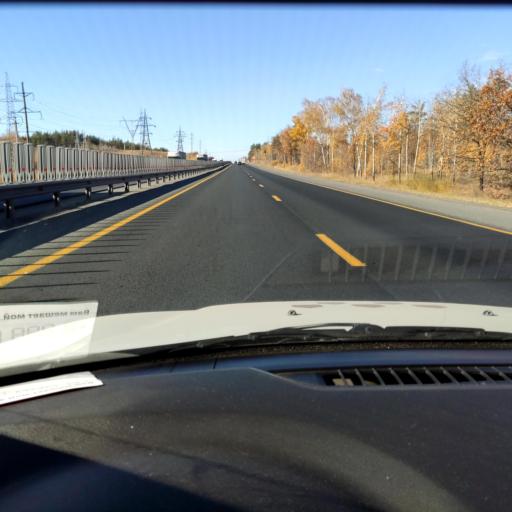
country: RU
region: Samara
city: Pribrezhnyy
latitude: 53.5131
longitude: 49.9146
